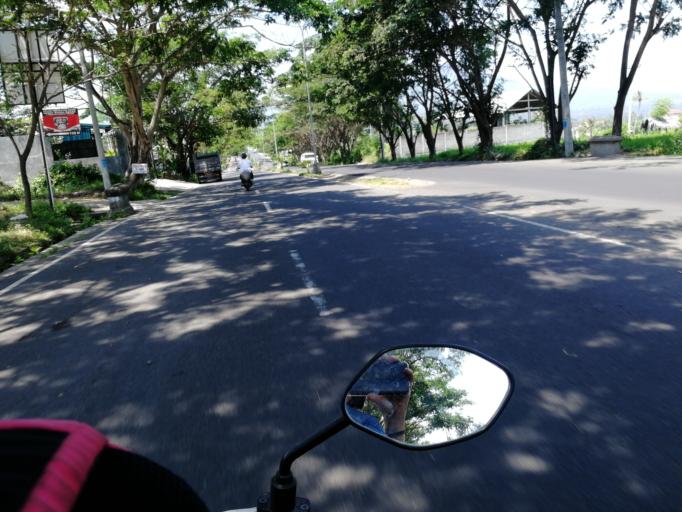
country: ID
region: Bali
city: Banjar Beji
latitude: -8.4453
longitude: 115.5889
